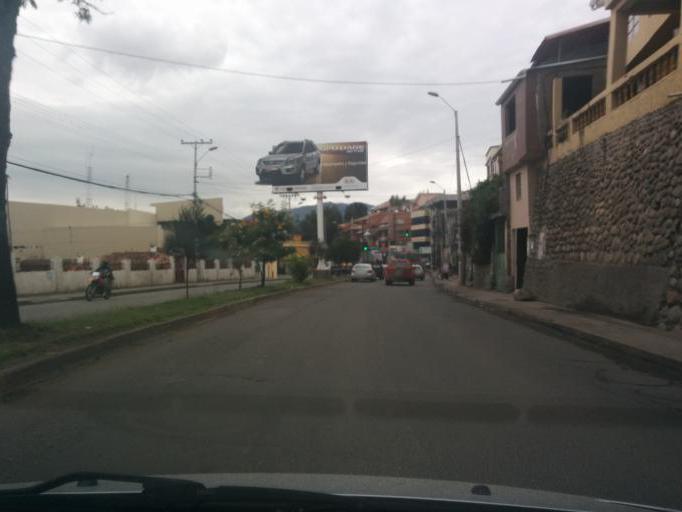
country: EC
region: Azuay
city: Cuenca
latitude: -2.8968
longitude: -78.9754
